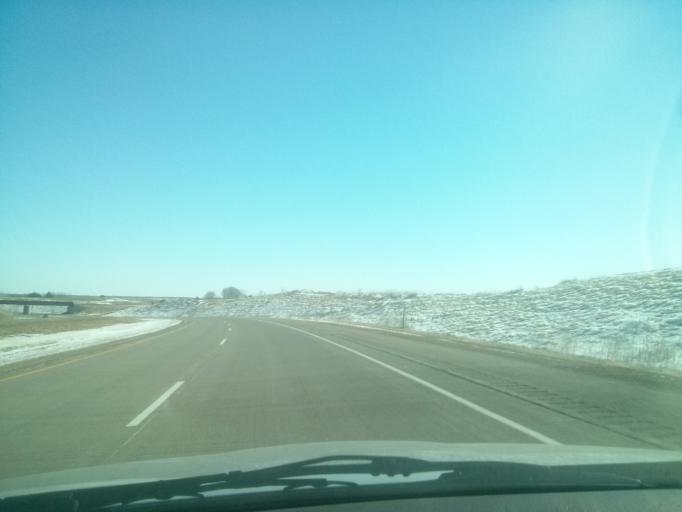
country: US
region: Wisconsin
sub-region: Saint Croix County
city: Somerset
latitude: 45.1091
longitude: -92.6717
